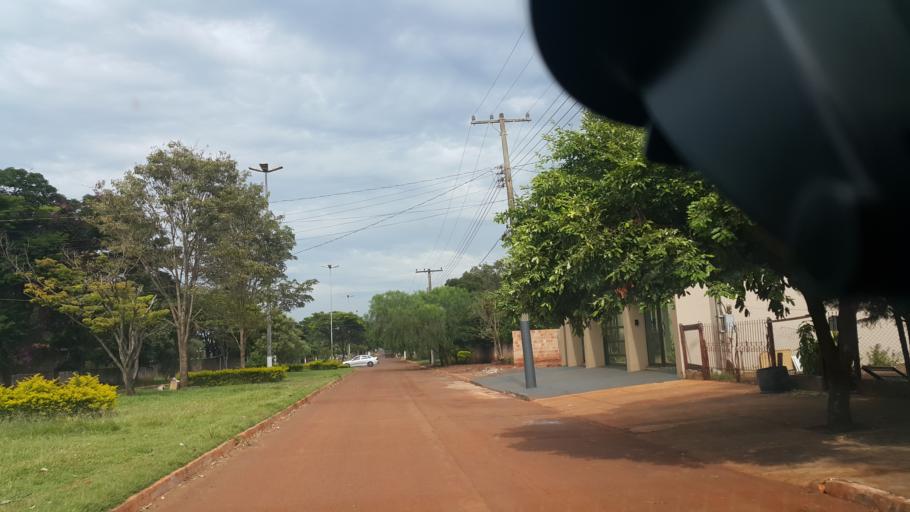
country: BR
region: Mato Grosso do Sul
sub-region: Dourados
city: Dourados
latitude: -22.0769
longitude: -54.7859
